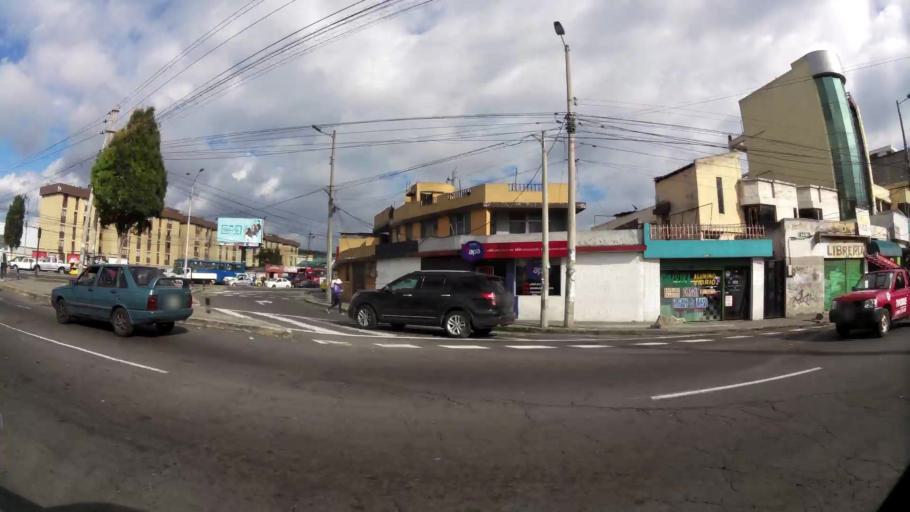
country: EC
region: Pichincha
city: Quito
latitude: -0.1545
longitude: -78.4773
